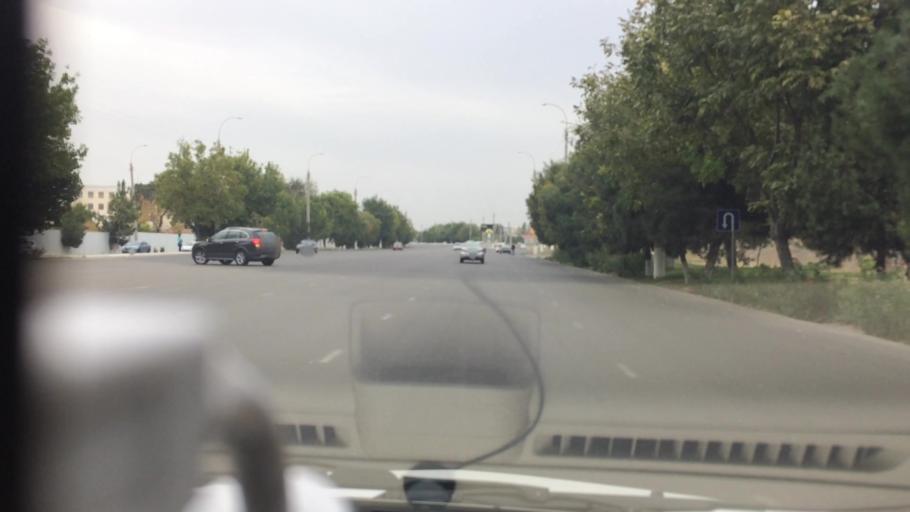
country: UZ
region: Toshkent
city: Salor
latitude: 41.3146
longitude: 69.3091
